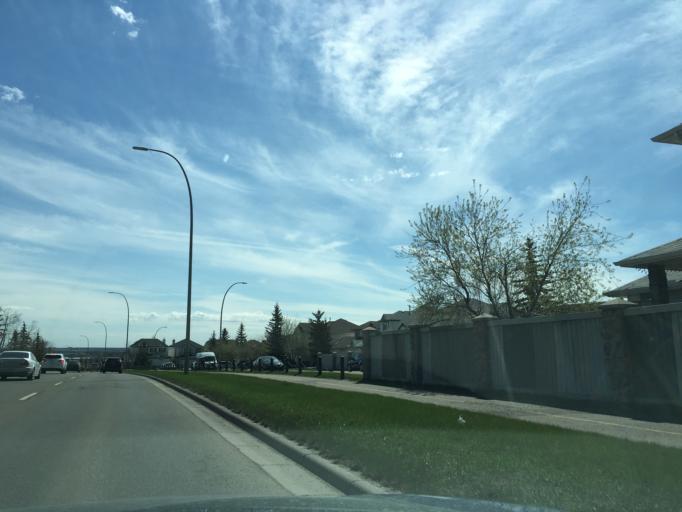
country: CA
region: Alberta
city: Calgary
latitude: 50.9028
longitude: -114.0840
